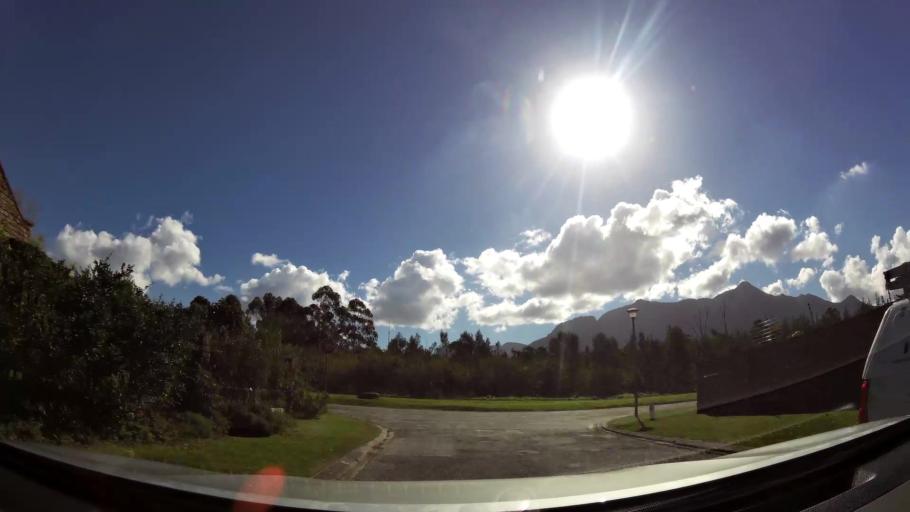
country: ZA
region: Western Cape
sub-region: Eden District Municipality
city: George
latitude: -33.9472
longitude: 22.4285
